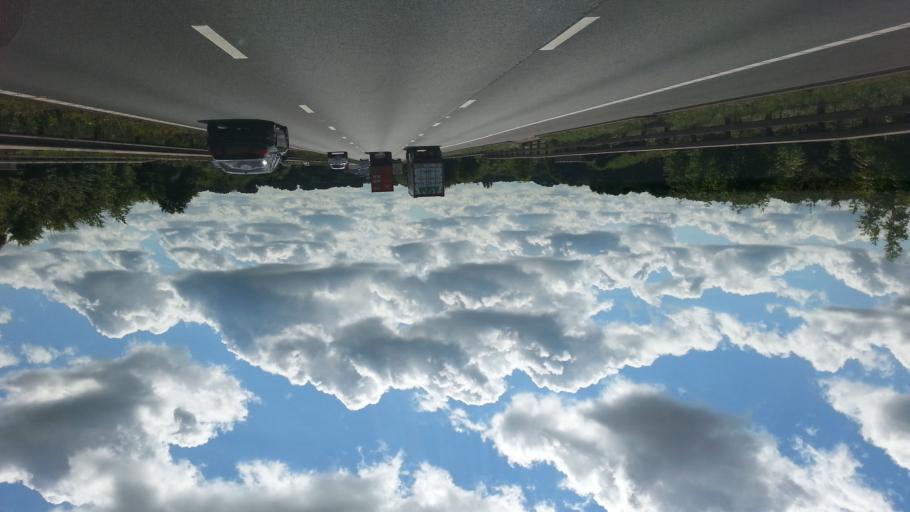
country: GB
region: England
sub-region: Leicestershire
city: Narborough
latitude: 52.5744
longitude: -1.1954
